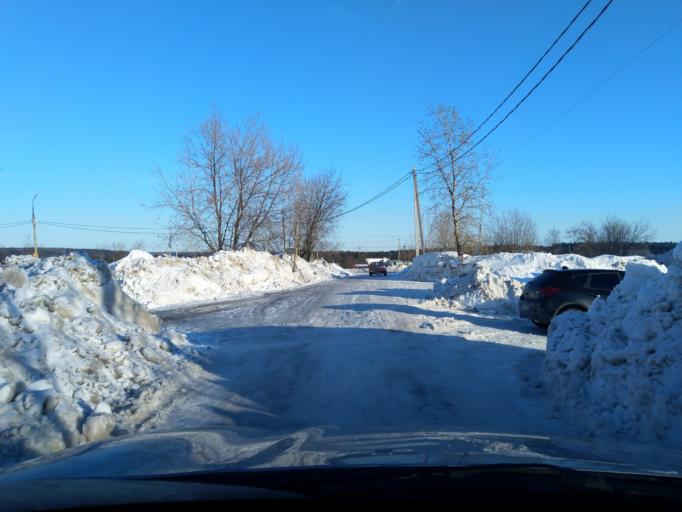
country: RU
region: Perm
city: Polazna
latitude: 58.2900
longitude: 56.4116
